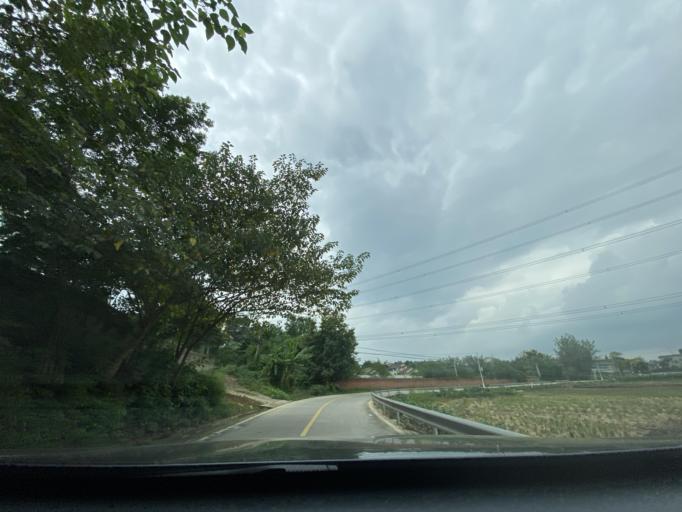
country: CN
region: Sichuan
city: Wujin
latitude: 30.3743
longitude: 103.9689
